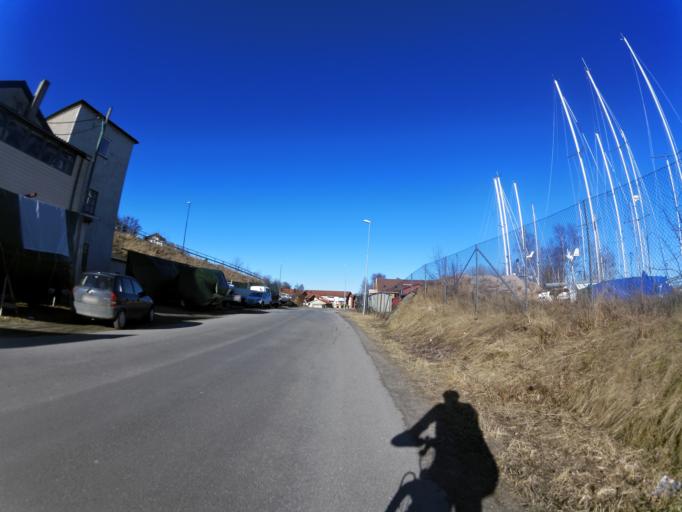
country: NO
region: Ostfold
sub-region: Fredrikstad
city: Fredrikstad
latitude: 59.2122
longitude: 10.9069
